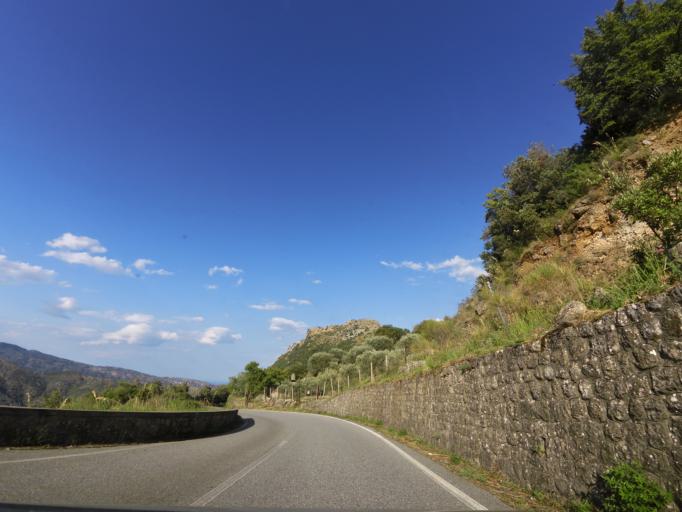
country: IT
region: Calabria
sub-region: Provincia di Reggio Calabria
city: Pazzano
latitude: 38.4740
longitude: 16.4472
